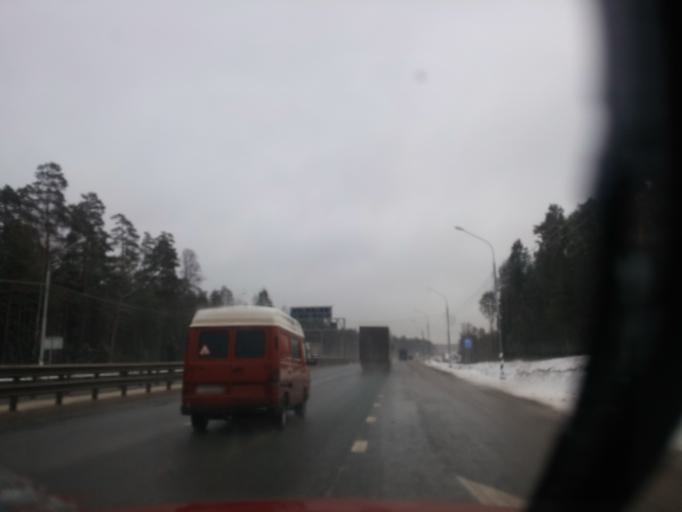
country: RU
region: Tverskaya
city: Likhoslavl'
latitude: 56.9426
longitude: 35.5051
